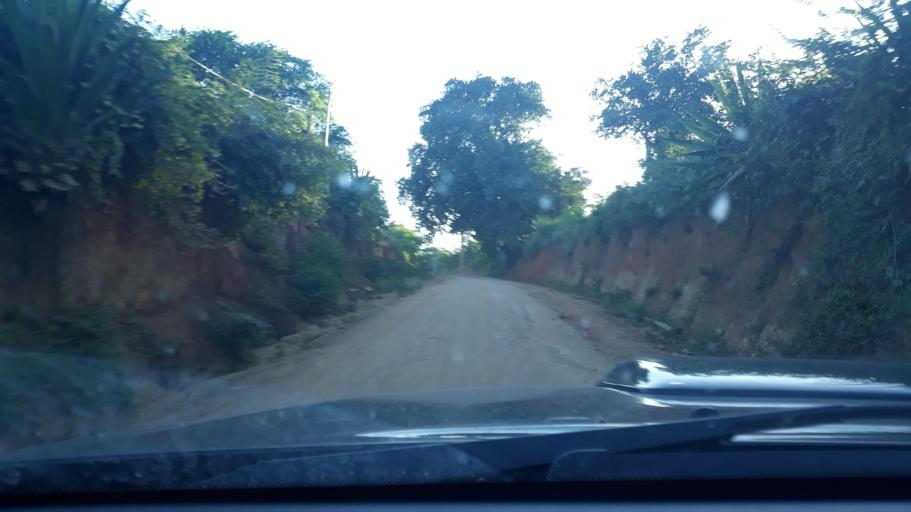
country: BR
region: Bahia
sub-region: Riacho De Santana
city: Riacho de Santana
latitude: -13.8245
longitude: -42.7261
